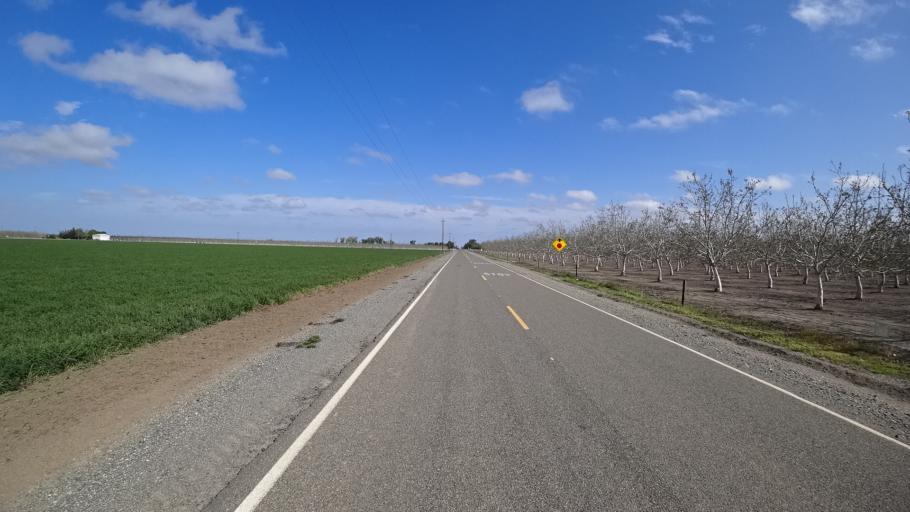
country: US
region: California
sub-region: Butte County
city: Biggs
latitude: 39.4615
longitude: -121.9302
